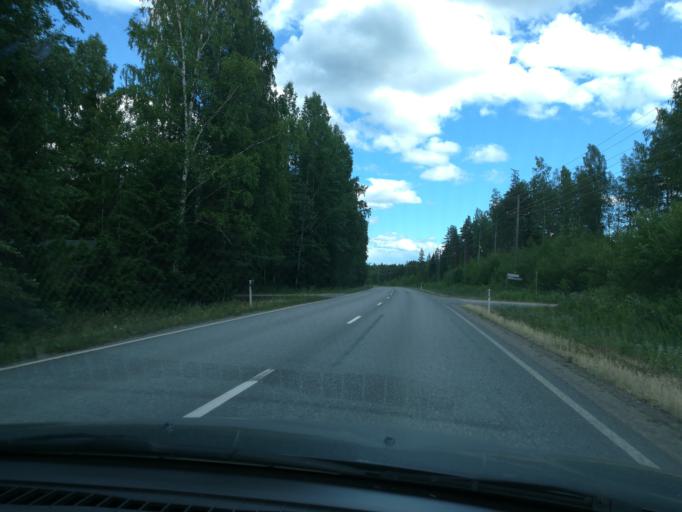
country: FI
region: Southern Savonia
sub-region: Mikkeli
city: Hirvensalmi
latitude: 61.6685
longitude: 26.8135
